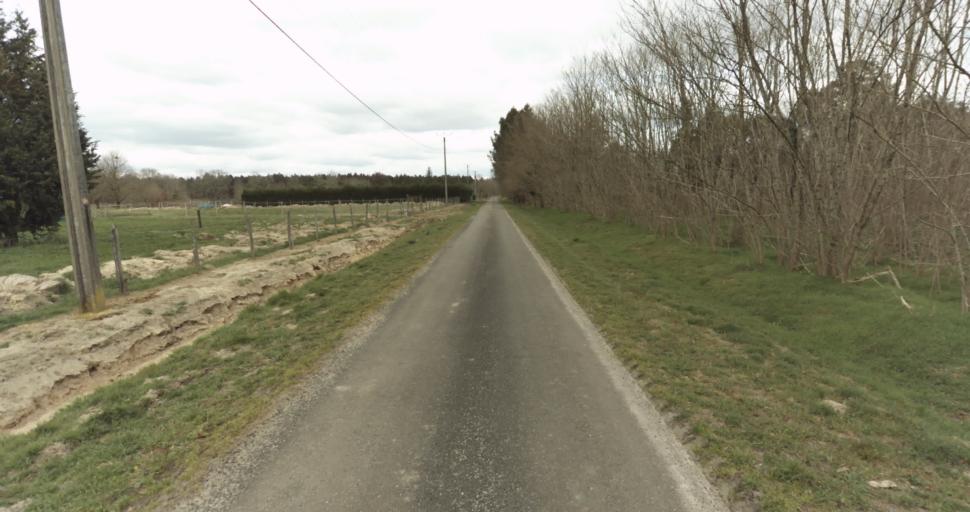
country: FR
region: Aquitaine
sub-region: Departement des Landes
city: Roquefort
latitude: 44.0697
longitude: -0.3831
